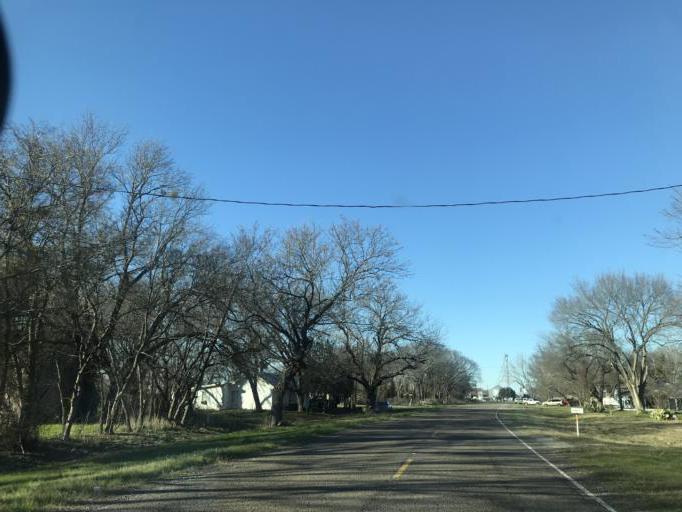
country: US
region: Texas
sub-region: Ellis County
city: Ferris
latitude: 32.4880
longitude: -96.6662
